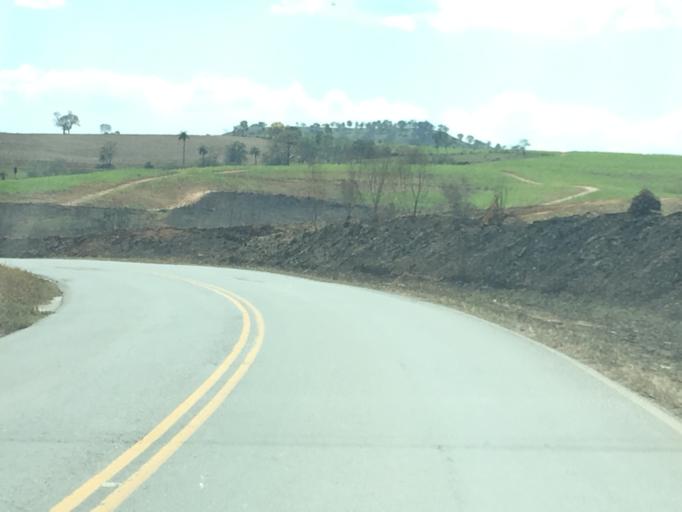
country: BR
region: Sao Paulo
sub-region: Moji-Guacu
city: Mogi-Gaucu
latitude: -22.3584
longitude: -46.8686
